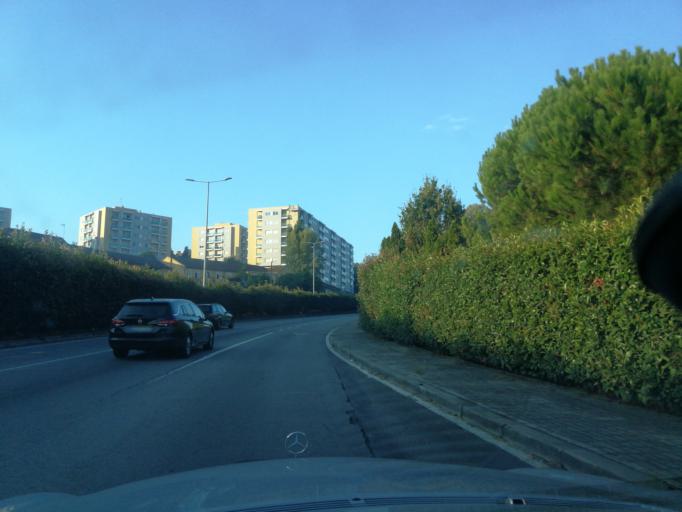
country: PT
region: Braga
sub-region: Braga
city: Braga
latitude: 41.5405
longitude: -8.4041
